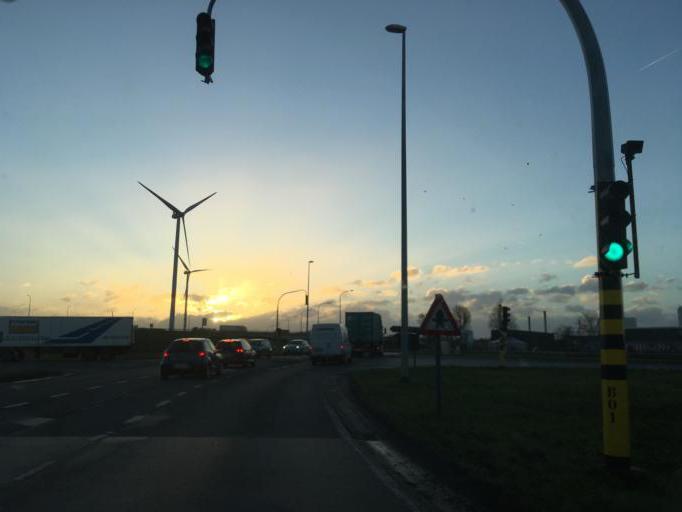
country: BE
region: Flanders
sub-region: Provincie West-Vlaanderen
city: Roeselare
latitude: 50.9386
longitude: 3.1687
